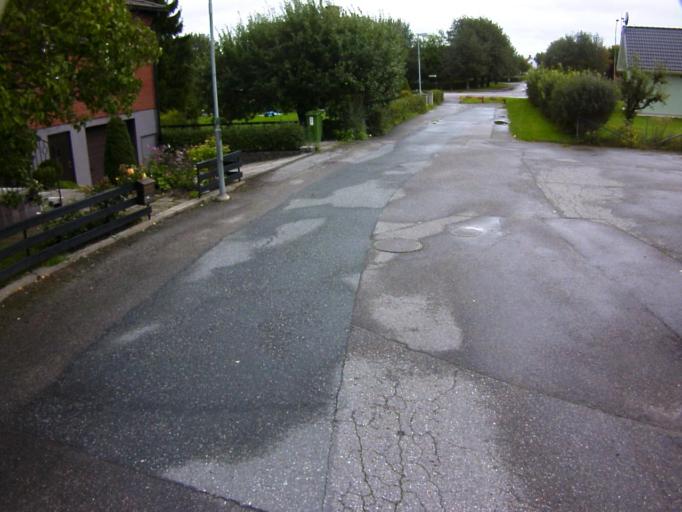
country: SE
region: Soedermanland
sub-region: Eskilstuna Kommun
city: Eskilstuna
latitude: 59.3770
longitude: 16.4708
